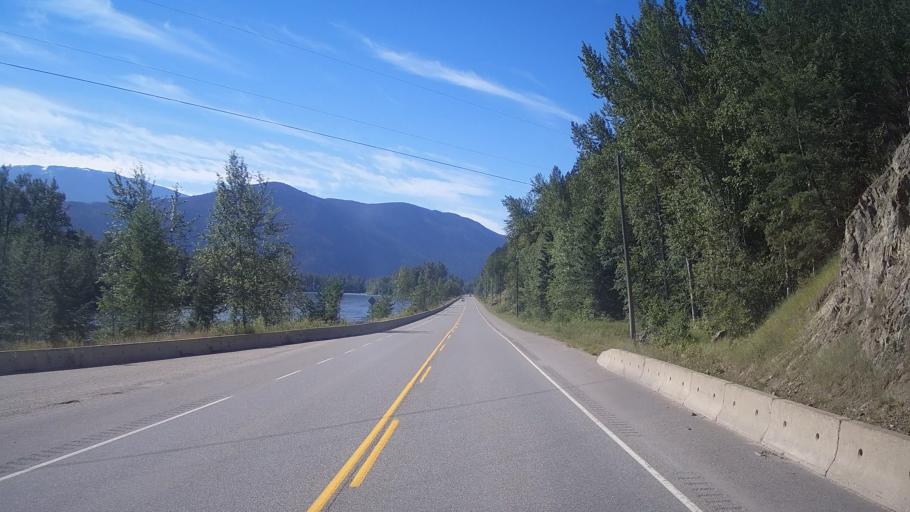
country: CA
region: British Columbia
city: Chase
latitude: 51.5541
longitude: -120.1742
